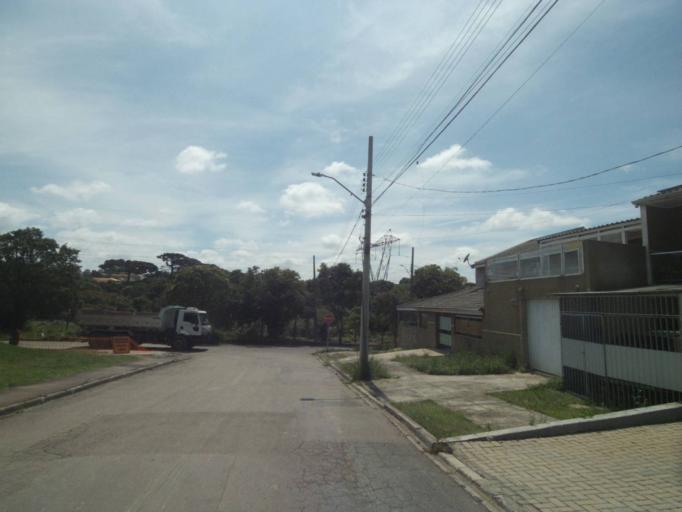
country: BR
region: Parana
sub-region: Curitiba
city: Curitiba
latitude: -25.4560
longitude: -49.3575
